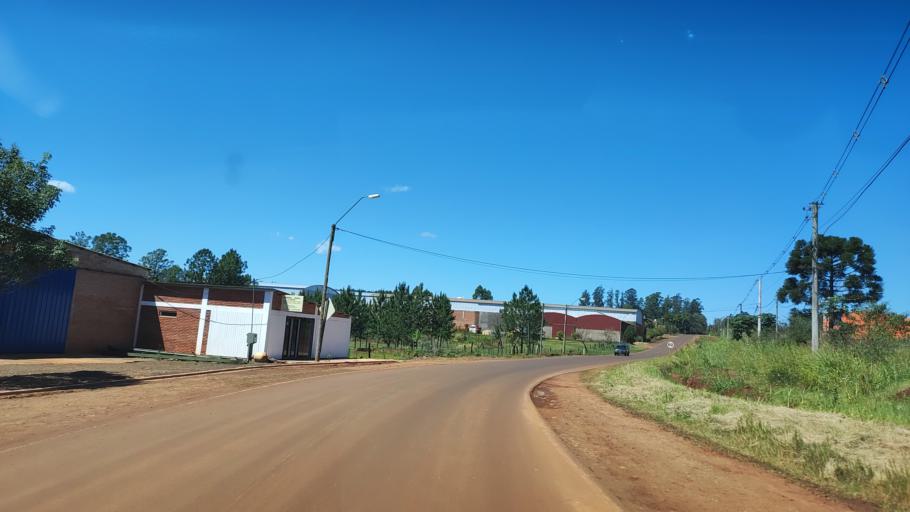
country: AR
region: Misiones
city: Puerto Rico
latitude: -26.8162
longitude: -55.0078
